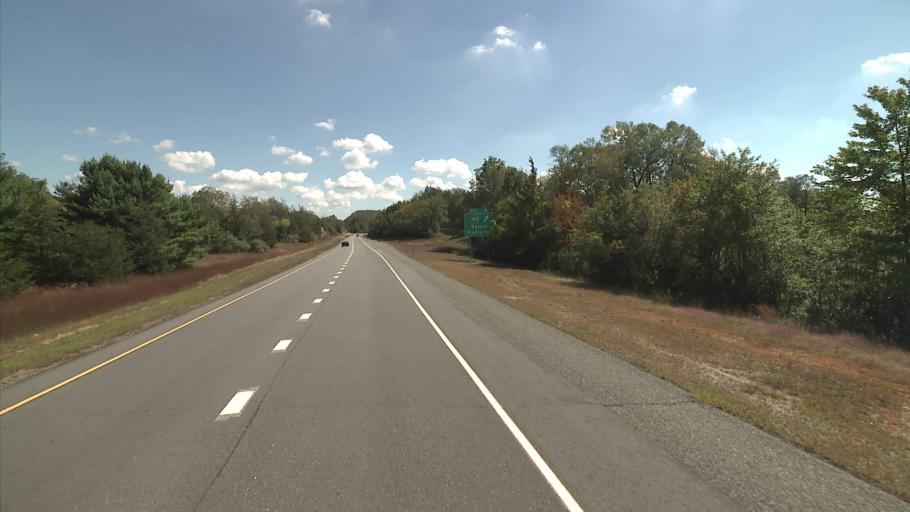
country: US
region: Connecticut
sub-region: New London County
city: Colchester
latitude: 41.4689
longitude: -72.2865
